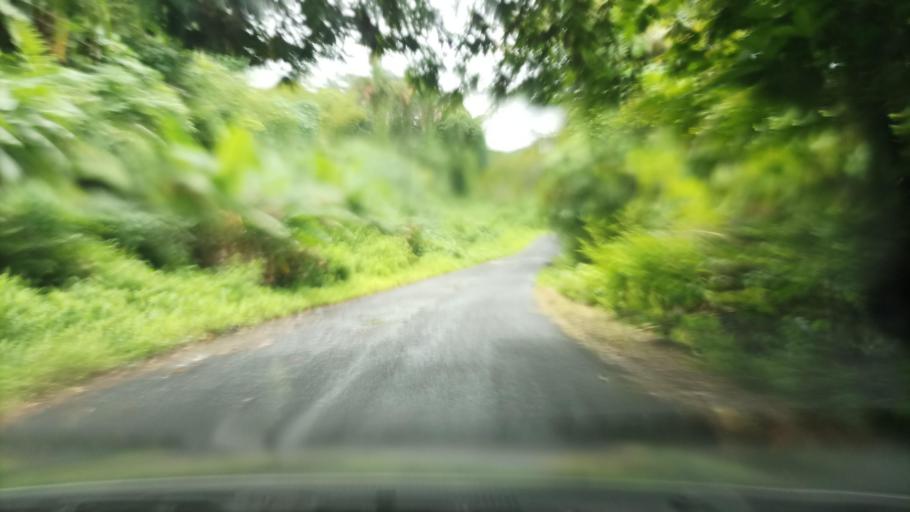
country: FM
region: Pohnpei
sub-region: Madolenihm Municipality
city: Madolenihm Municipality Government
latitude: 6.8489
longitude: 158.3002
